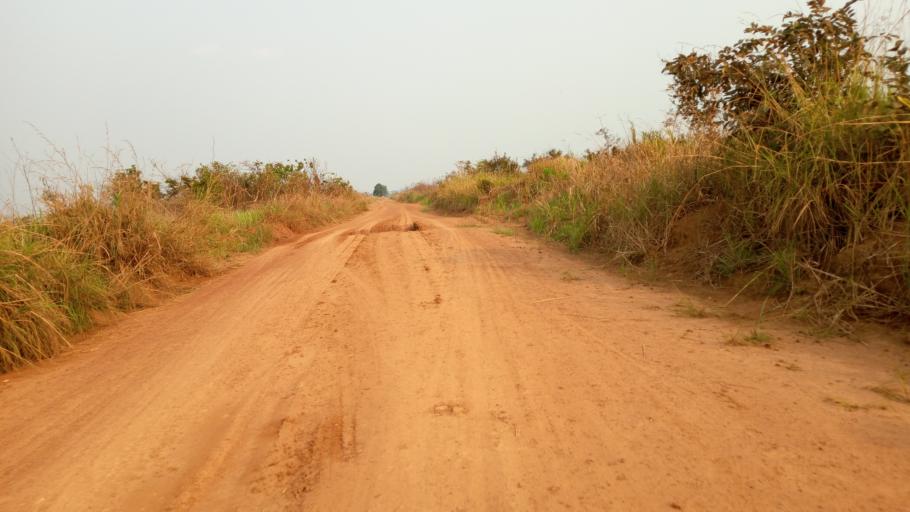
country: CD
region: Bandundu
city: Bandundu
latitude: -3.4082
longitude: 17.5944
